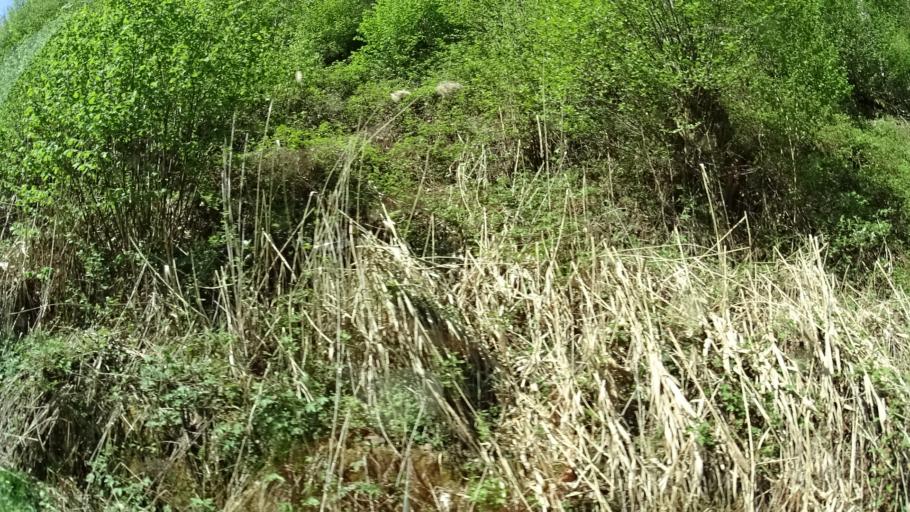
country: DE
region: Baden-Wuerttemberg
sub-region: Karlsruhe Region
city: Hofen an der Enz
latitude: 48.7985
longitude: 8.5529
